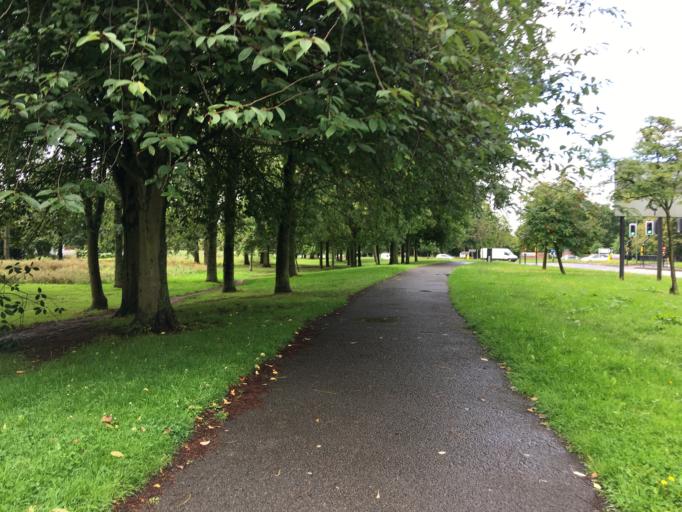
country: GB
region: England
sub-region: Coventry
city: Coventry
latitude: 52.3902
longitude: -1.5546
